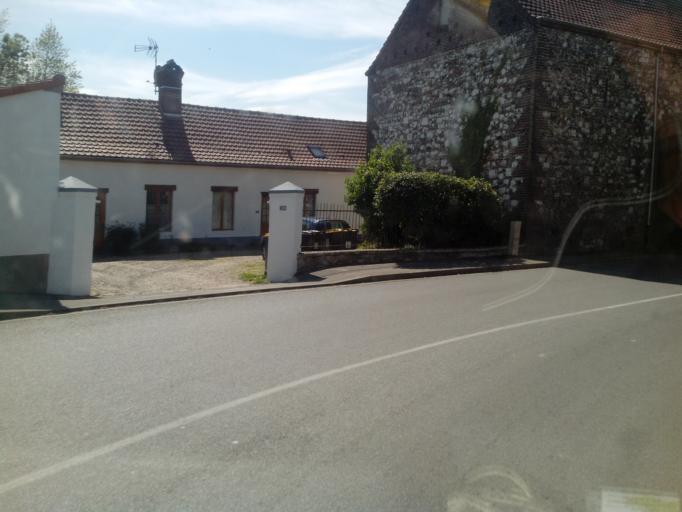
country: FR
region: Nord-Pas-de-Calais
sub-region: Departement du Pas-de-Calais
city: Montreuil
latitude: 50.4872
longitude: 1.7424
